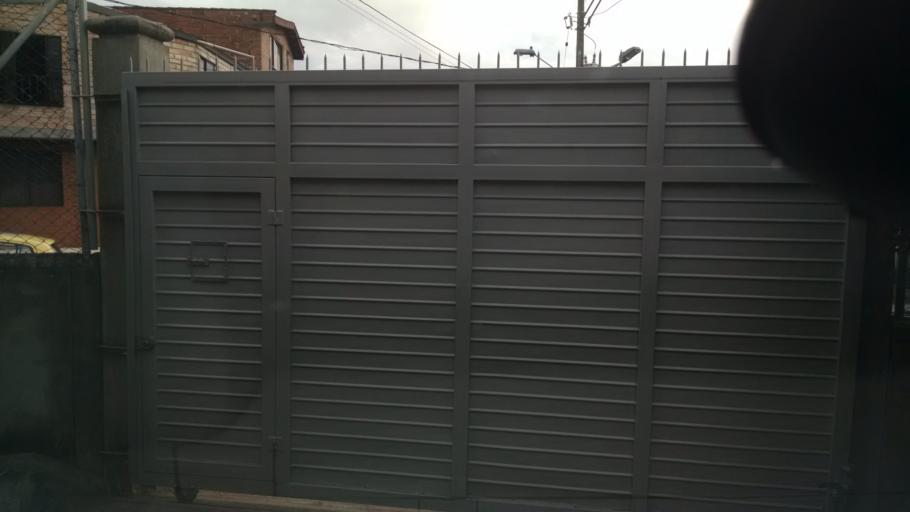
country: CO
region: Antioquia
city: Medellin
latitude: 6.2833
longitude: -75.5919
